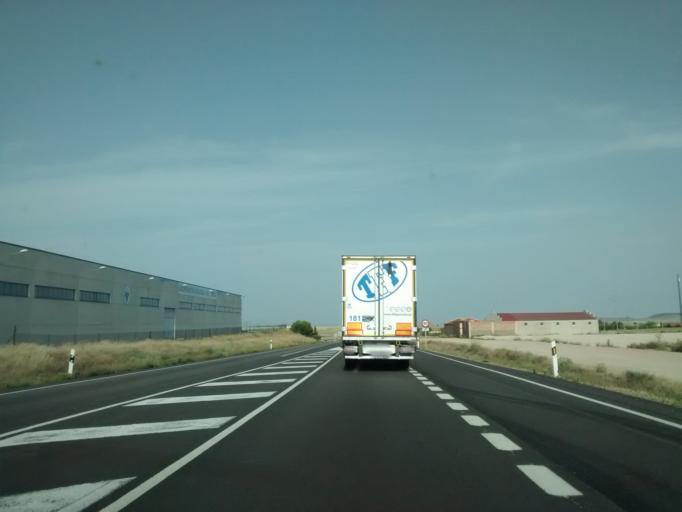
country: ES
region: Aragon
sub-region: Provincia de Zaragoza
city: Albeta
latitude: 41.8310
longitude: -1.5062
